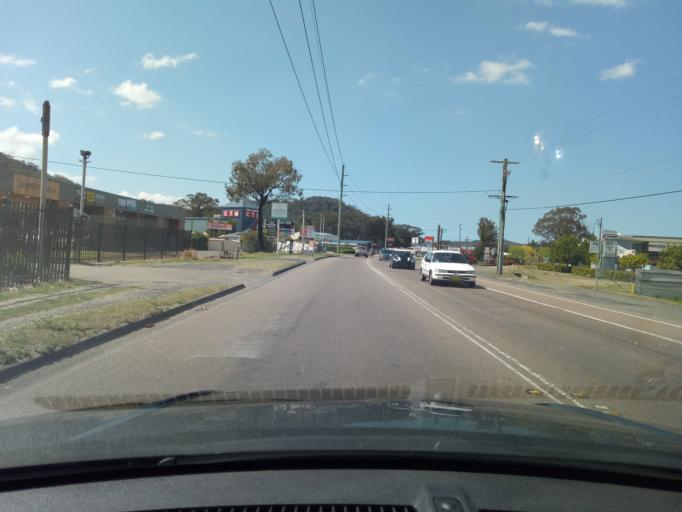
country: AU
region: New South Wales
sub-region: Gosford Shire
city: Gosford
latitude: -33.4178
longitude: 151.3219
